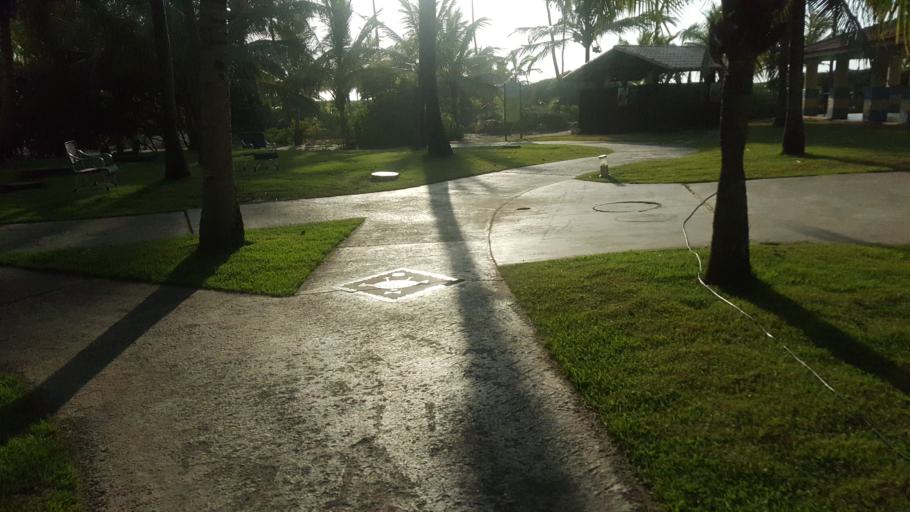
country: BR
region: Bahia
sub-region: Mata De Sao Joao
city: Mata de Sao Joao
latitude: -12.4389
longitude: -37.9169
